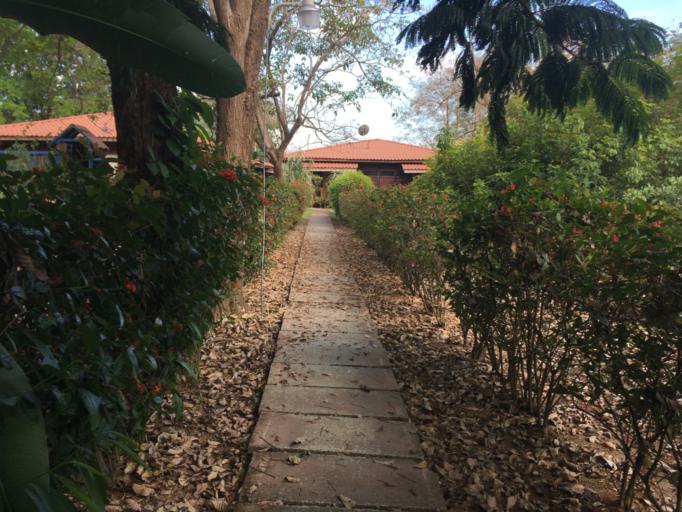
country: CR
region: San Jose
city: Daniel Flores
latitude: 9.1619
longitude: -83.7454
